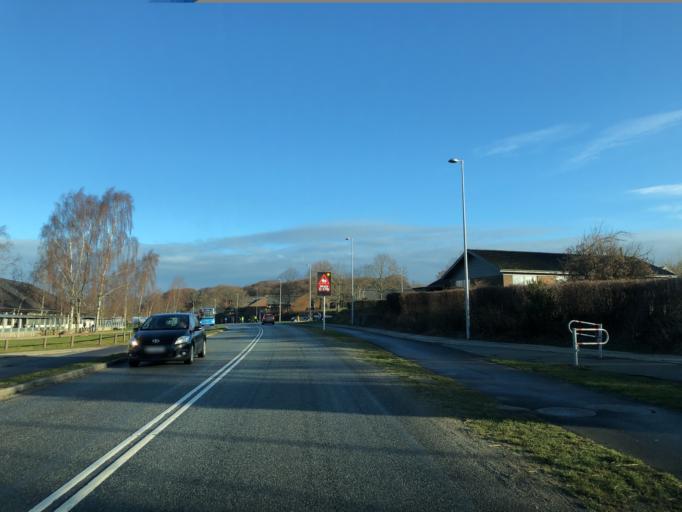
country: DK
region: Central Jutland
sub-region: Favrskov Kommune
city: Hinnerup
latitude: 56.2587
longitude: 10.0705
